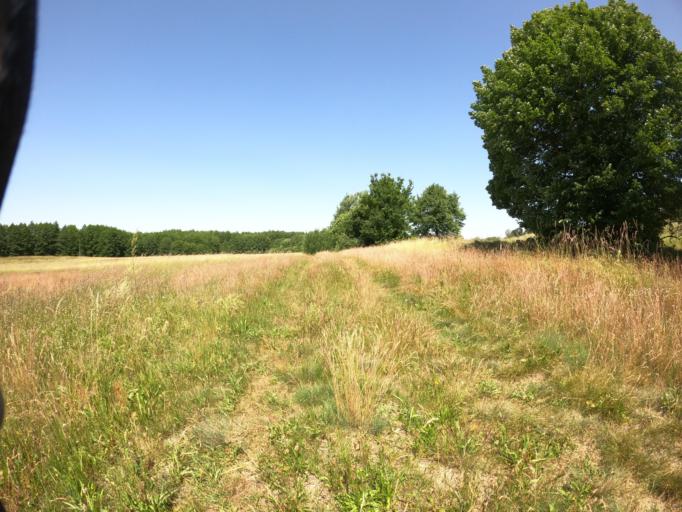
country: PL
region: West Pomeranian Voivodeship
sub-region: Powiat mysliborski
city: Mysliborz
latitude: 52.8921
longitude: 14.8083
